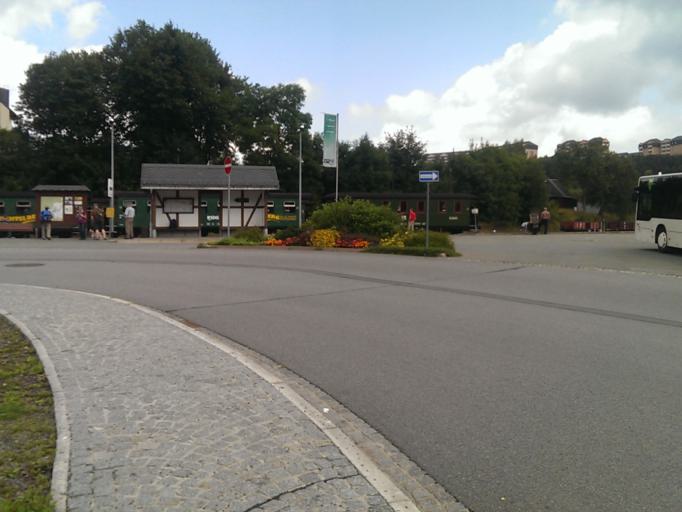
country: DE
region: Saxony
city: Kurort Oberwiesenthal
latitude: 50.4208
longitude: 12.9725
